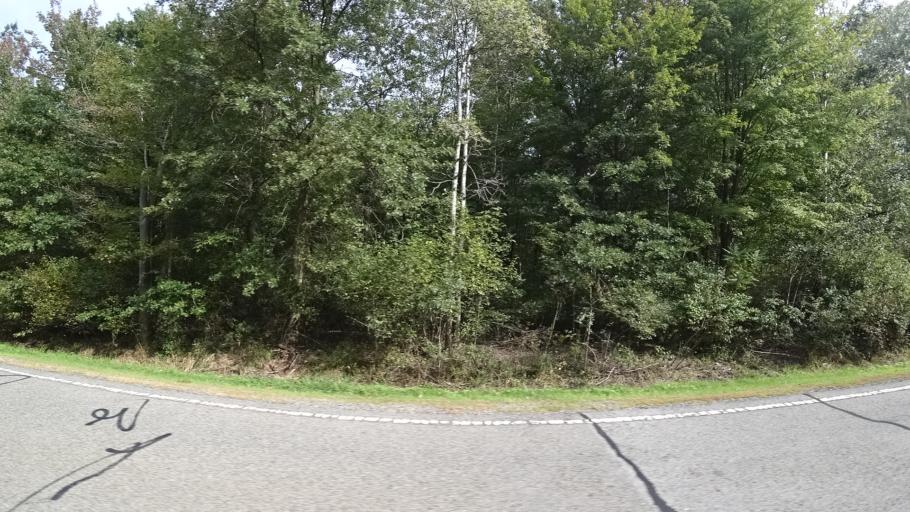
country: US
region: Indiana
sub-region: LaPorte County
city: Long Beach
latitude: 41.7325
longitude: -86.8361
